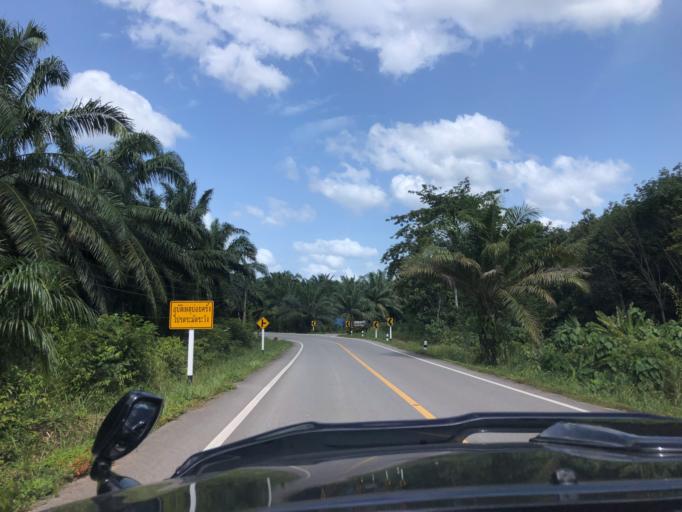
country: TH
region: Krabi
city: Khlong Thom
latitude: 7.9467
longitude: 99.2095
